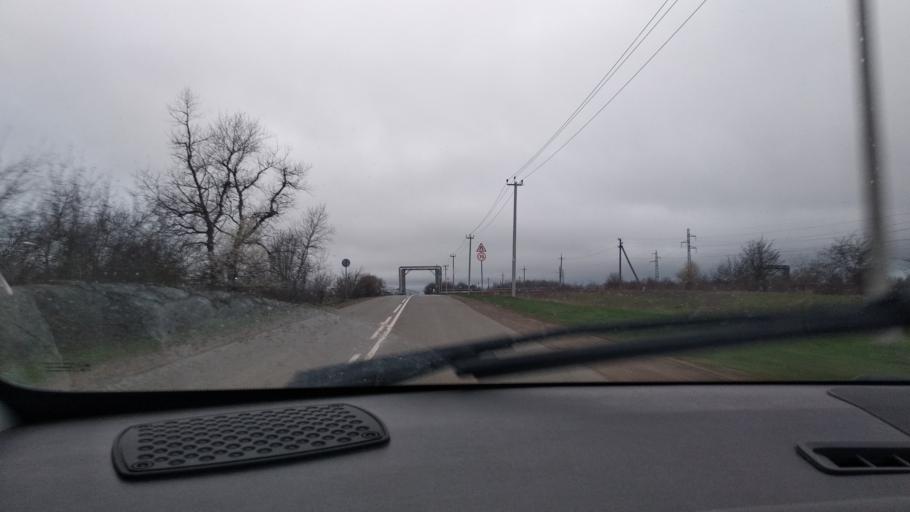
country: RU
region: Krasnodarskiy
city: Afipskiy
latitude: 44.8930
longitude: 38.8111
